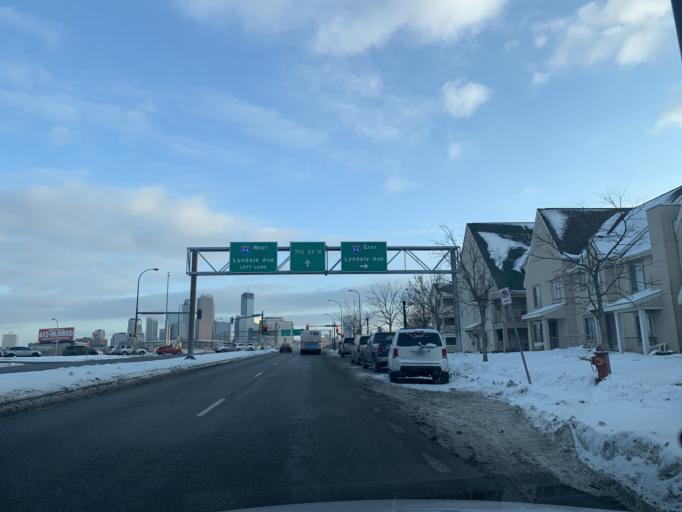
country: US
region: Minnesota
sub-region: Hennepin County
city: Minneapolis
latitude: 44.9890
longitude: -93.2903
